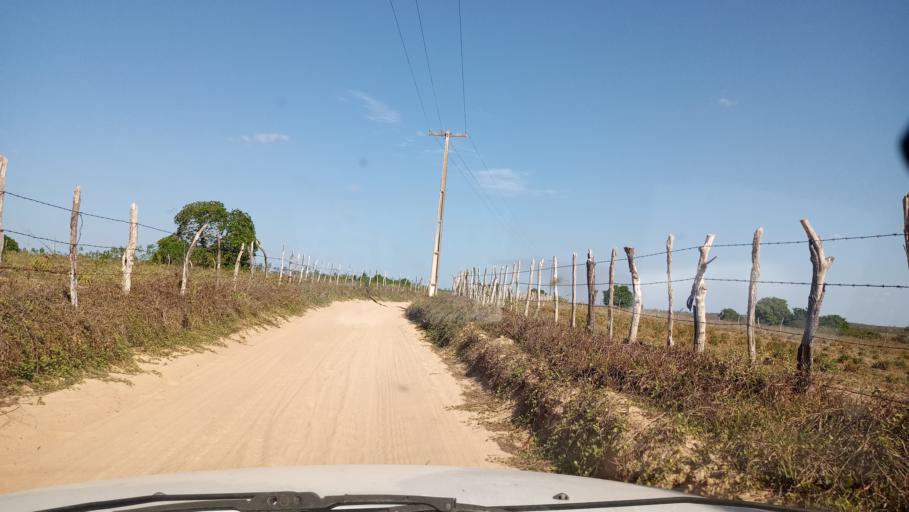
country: BR
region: Rio Grande do Norte
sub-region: Brejinho
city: Brejinho
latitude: -6.1768
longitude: -35.4574
